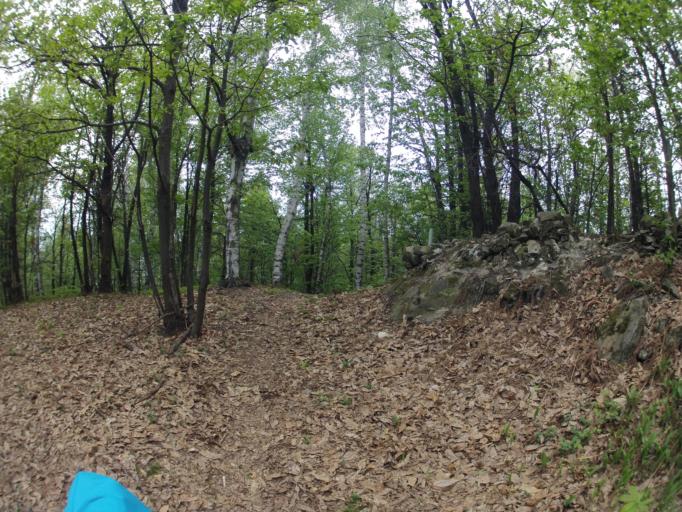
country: IT
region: Piedmont
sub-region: Provincia di Cuneo
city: Peveragno
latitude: 44.3258
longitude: 7.5931
